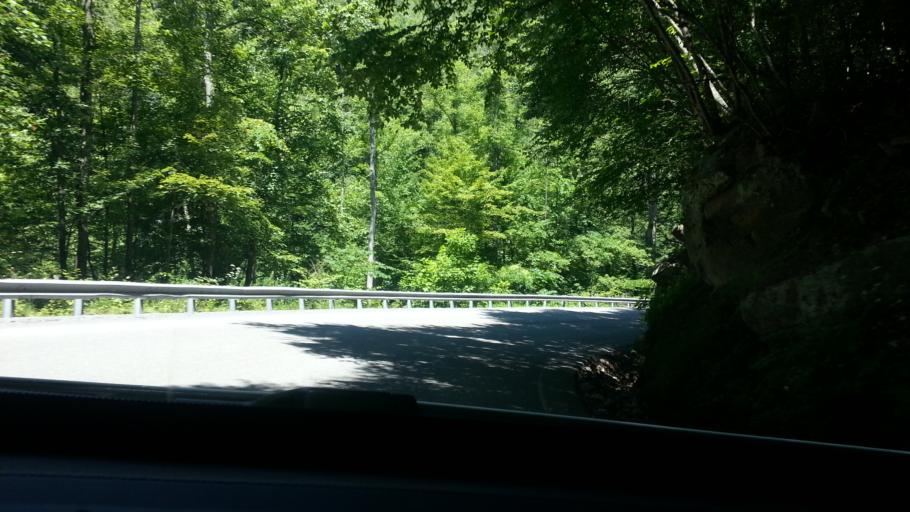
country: US
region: West Virginia
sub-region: Fayette County
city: Ansted
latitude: 38.1069
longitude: -81.1495
